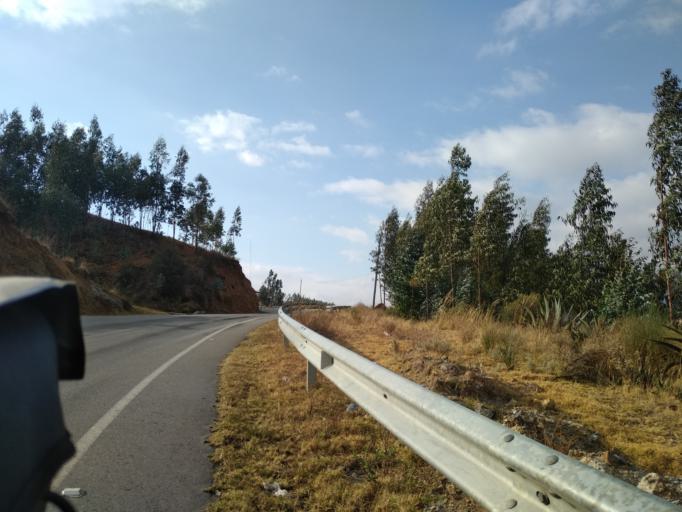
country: PE
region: La Libertad
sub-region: Provincia de Otuzco
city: Agallpampa
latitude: -7.9874
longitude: -78.5346
